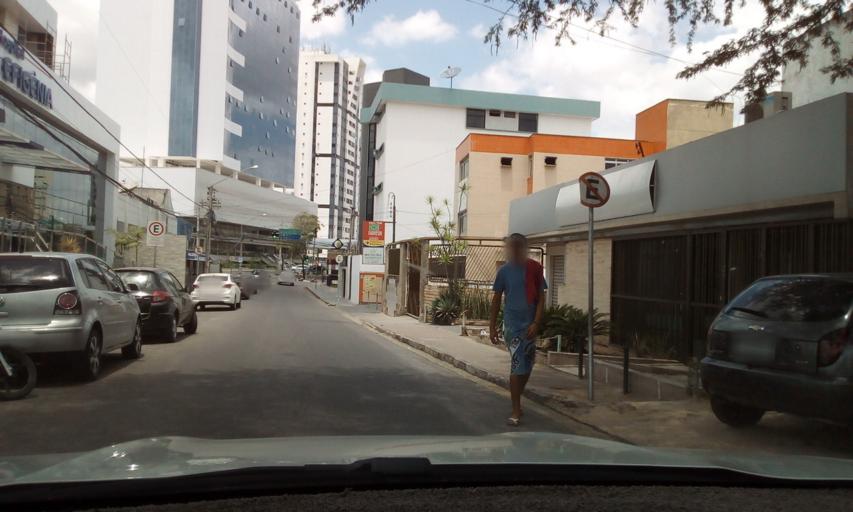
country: BR
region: Pernambuco
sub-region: Caruaru
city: Caruaru
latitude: -8.2706
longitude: -35.9767
